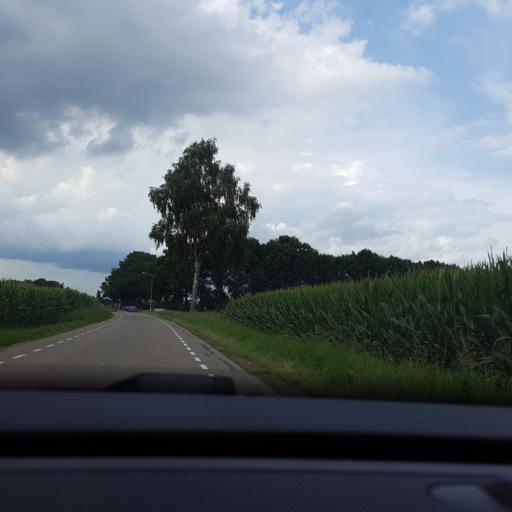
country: NL
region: Gelderland
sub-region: Gemeente Doesburg
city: Doesburg
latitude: 52.0209
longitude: 6.1659
